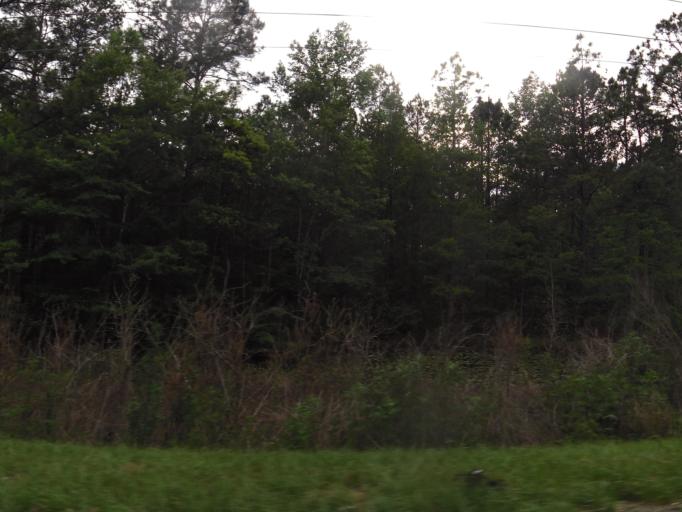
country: US
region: South Carolina
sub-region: Jasper County
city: Hardeeville
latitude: 32.3339
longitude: -81.0909
